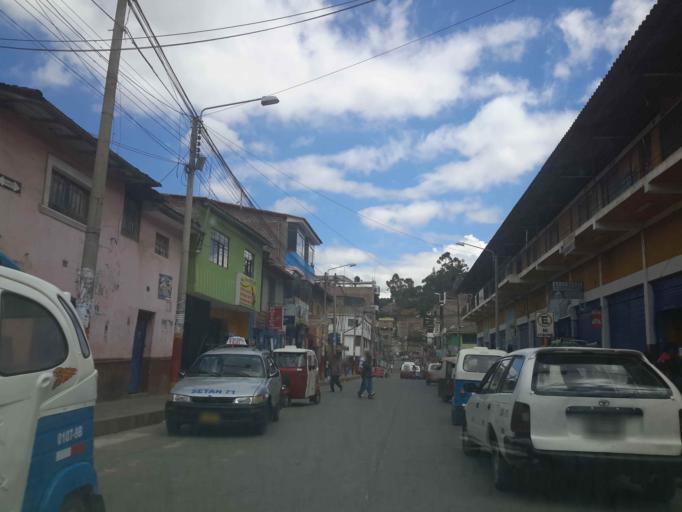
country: PE
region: Apurimac
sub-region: Provincia de Andahuaylas
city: Andahuaylas
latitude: -13.6551
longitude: -73.3872
